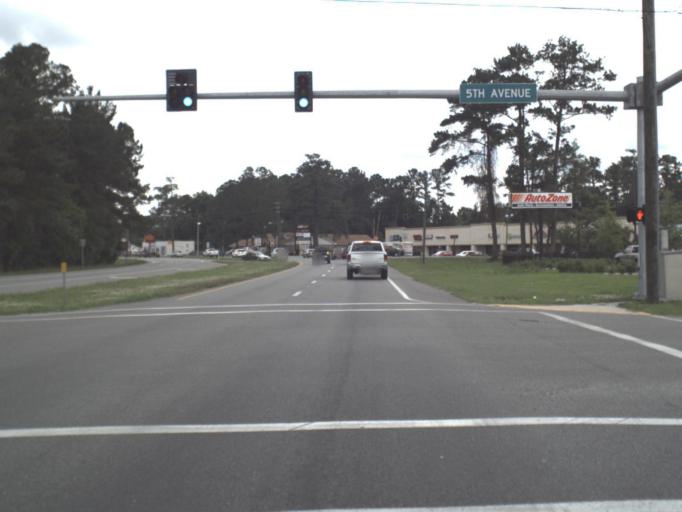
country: US
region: Florida
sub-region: Nassau County
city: Callahan
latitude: 30.5590
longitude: -81.8249
